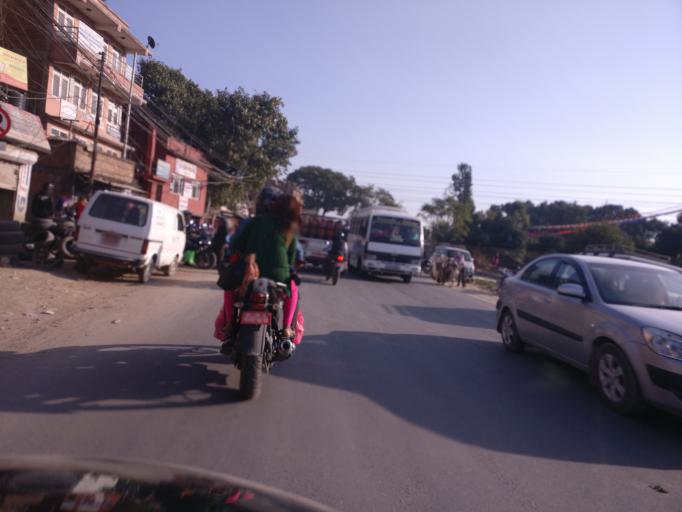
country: NP
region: Central Region
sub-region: Bagmati Zone
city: Patan
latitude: 27.6658
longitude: 85.3238
